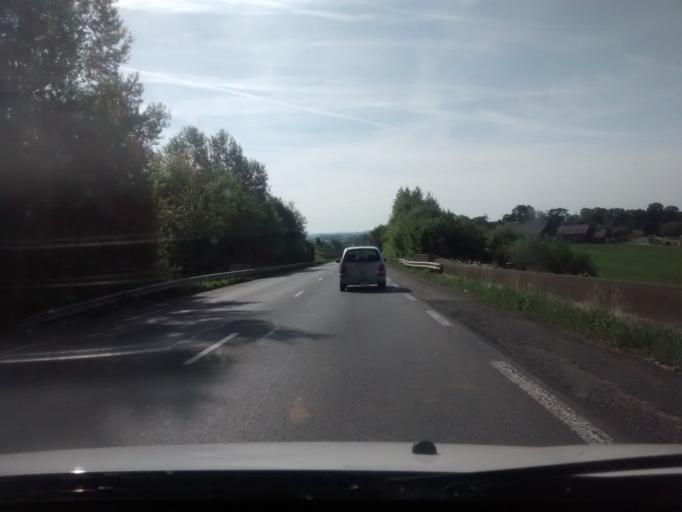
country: FR
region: Brittany
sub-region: Departement d'Ille-et-Vilaine
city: Lecousse
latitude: 48.3436
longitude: -1.2222
